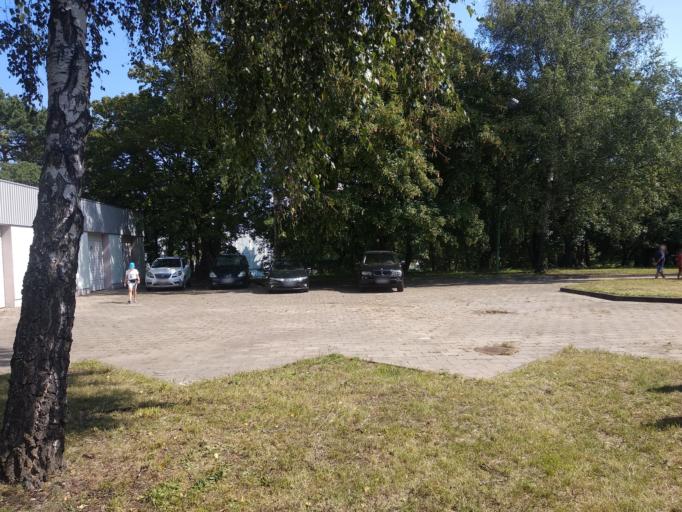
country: LT
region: Klaipedos apskritis
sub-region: Klaipeda
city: Klaipeda
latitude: 55.7276
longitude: 21.0959
